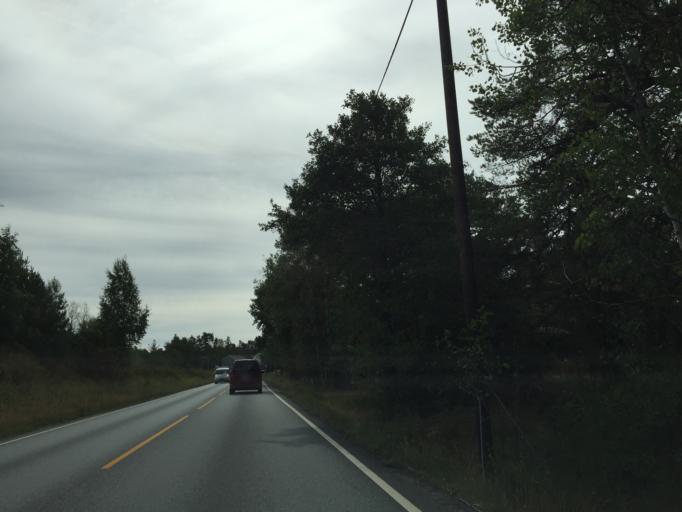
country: NO
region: Ostfold
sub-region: Fredrikstad
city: Fredrikstad
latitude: 59.1178
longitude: 10.9081
